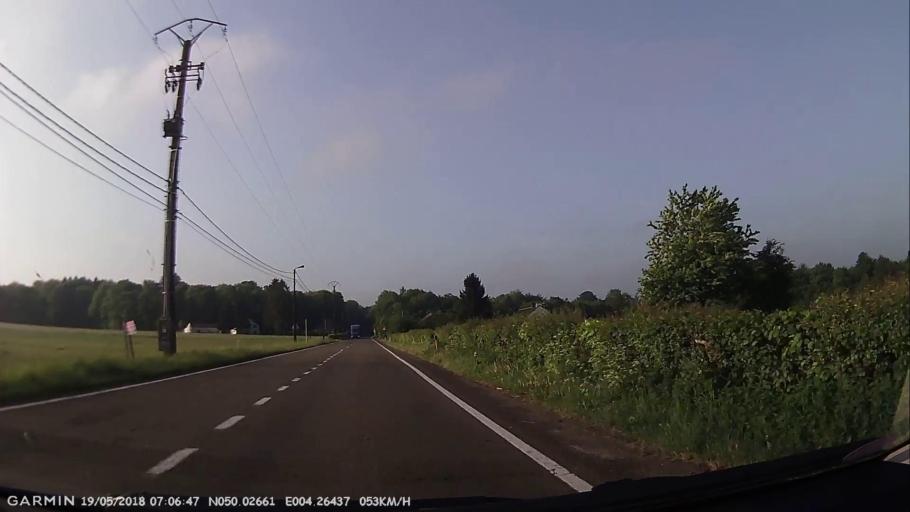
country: BE
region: Wallonia
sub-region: Province du Hainaut
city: Chimay
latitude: 50.0265
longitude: 4.2644
